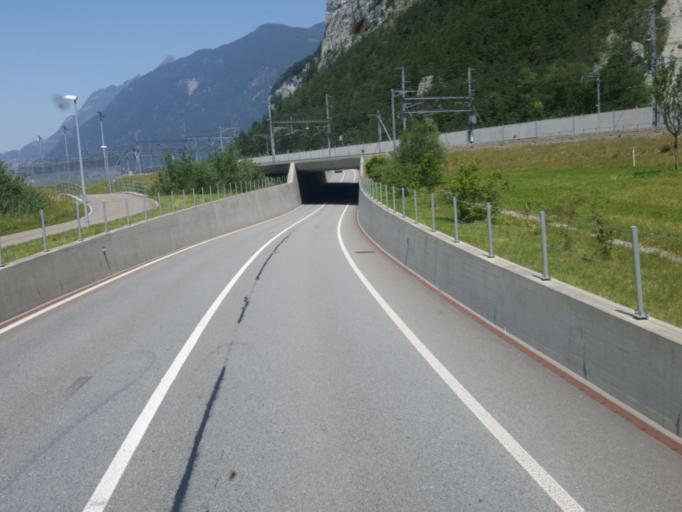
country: CH
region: Uri
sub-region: Uri
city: Erstfeld
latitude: 46.8382
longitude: 8.6443
